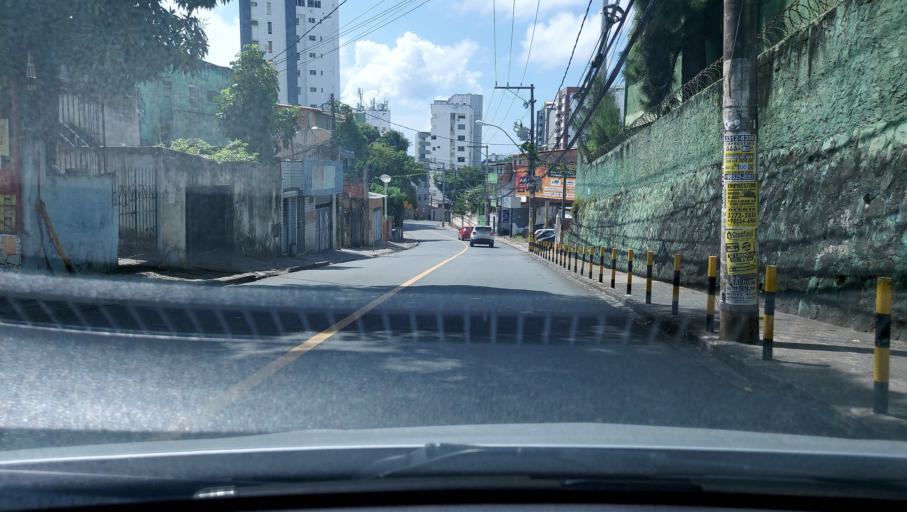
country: BR
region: Bahia
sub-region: Salvador
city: Salvador
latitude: -12.9915
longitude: -38.4777
